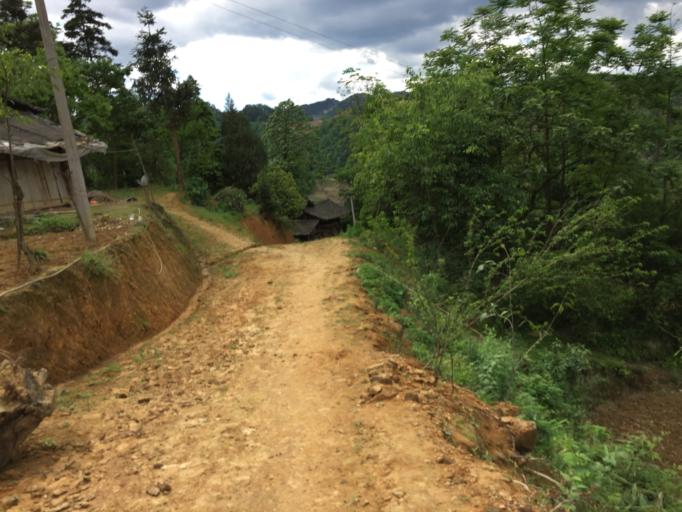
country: CN
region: Guizhou Sheng
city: Xujiaba
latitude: 27.6781
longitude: 108.0856
